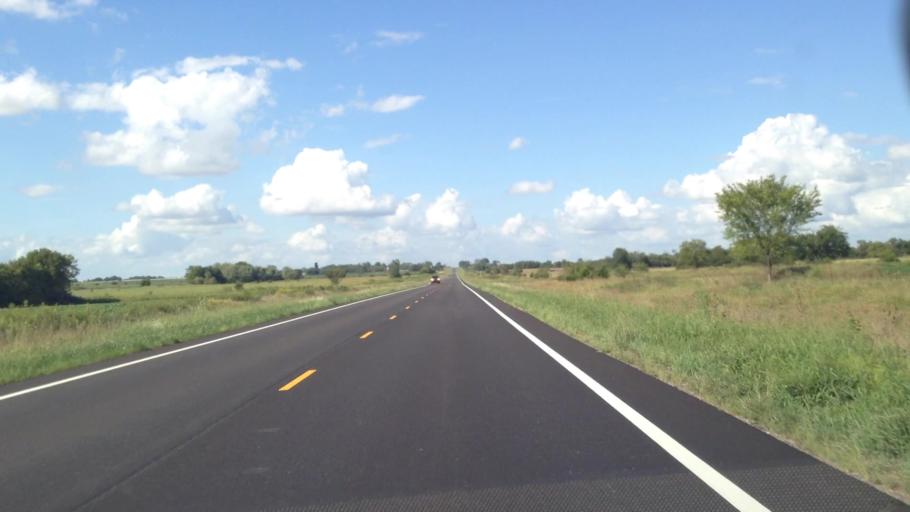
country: US
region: Kansas
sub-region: Neosho County
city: Erie
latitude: 37.7739
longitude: -95.1605
